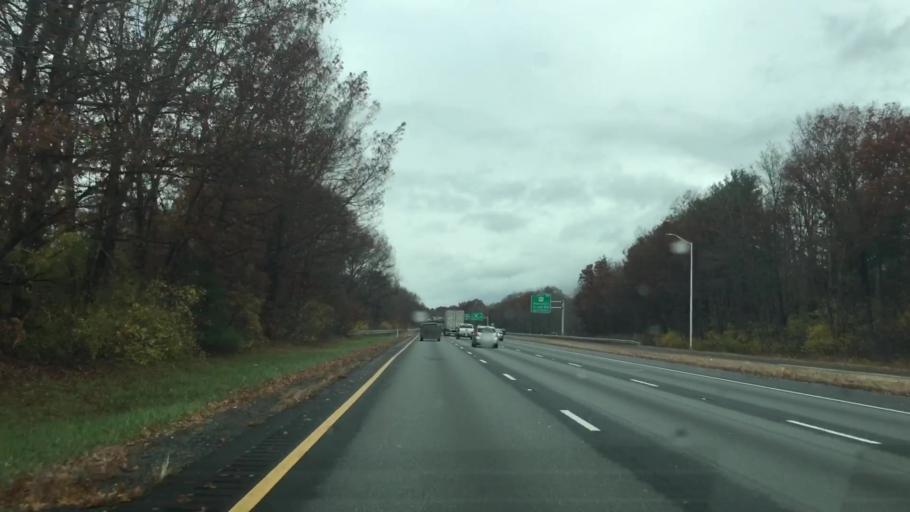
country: US
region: Massachusetts
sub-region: Essex County
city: Haverhill
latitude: 42.7761
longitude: -71.1176
